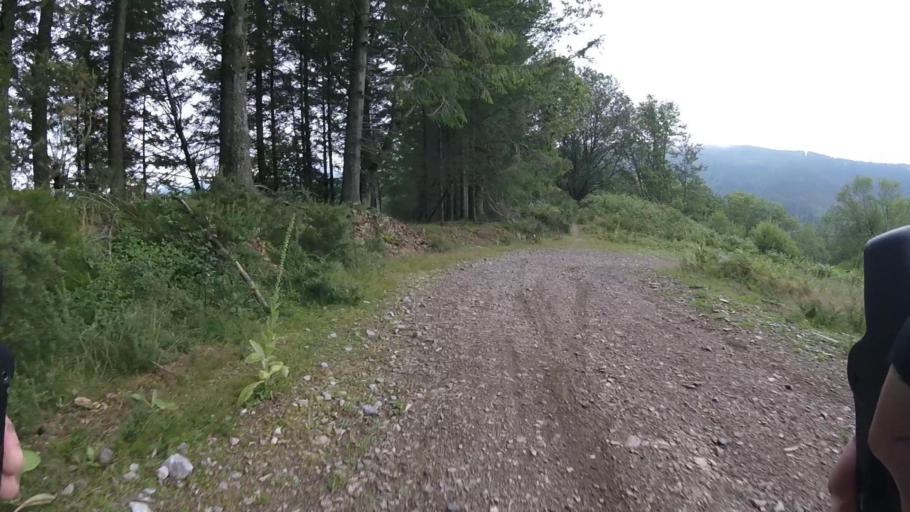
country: ES
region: Navarre
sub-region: Provincia de Navarra
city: Arano
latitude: 43.2540
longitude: -1.8723
